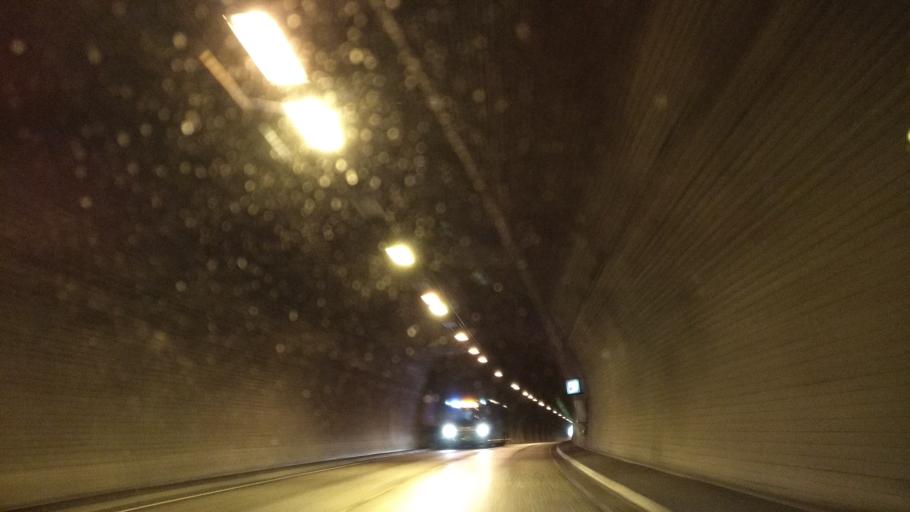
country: NO
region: Rogaland
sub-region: Stavanger
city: Stavanger
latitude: 58.9516
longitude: 5.7392
